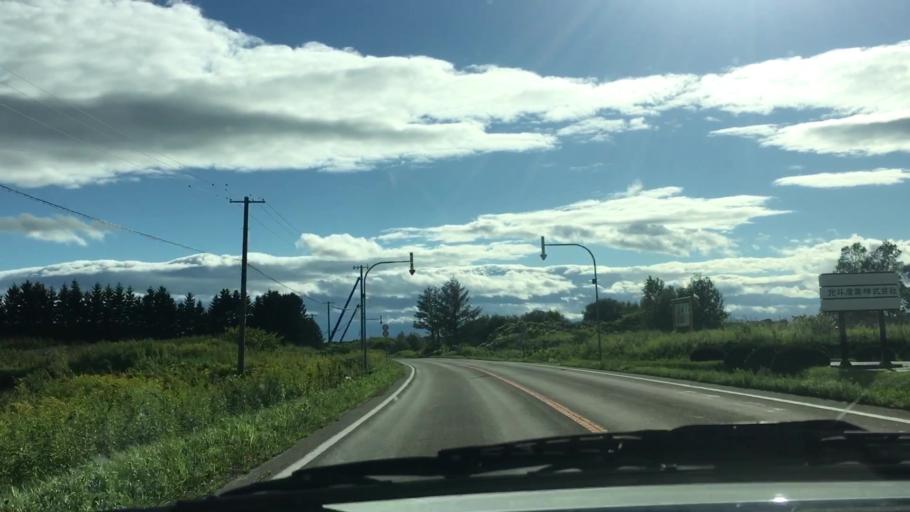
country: JP
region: Hokkaido
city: Otofuke
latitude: 43.1616
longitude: 143.2492
